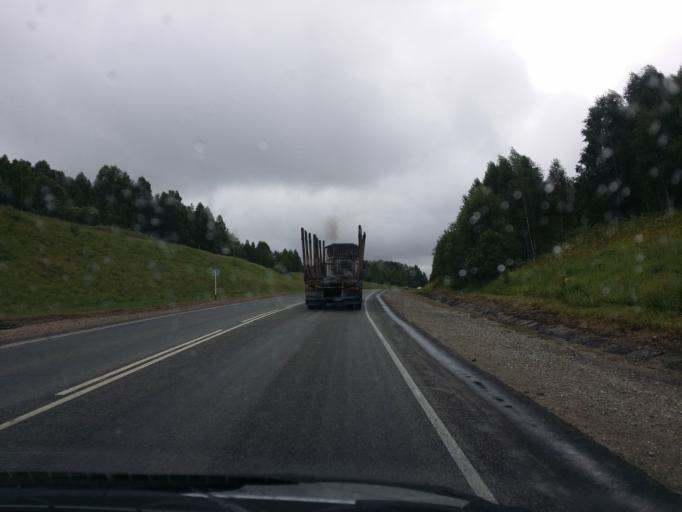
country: RU
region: Altai Krai
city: Nalobikha
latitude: 53.1531
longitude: 84.6980
